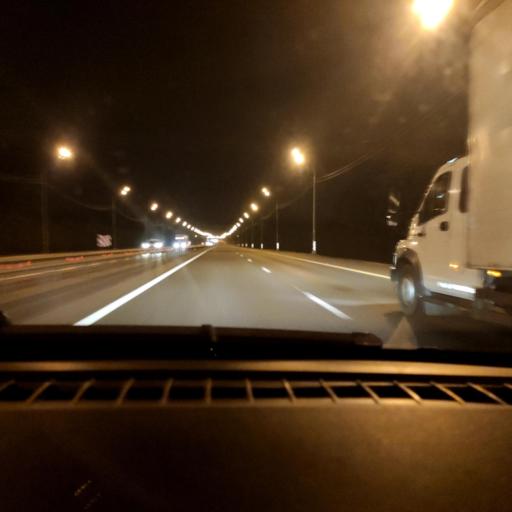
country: RU
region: Lipetsk
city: Khlevnoye
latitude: 52.1994
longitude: 39.1675
